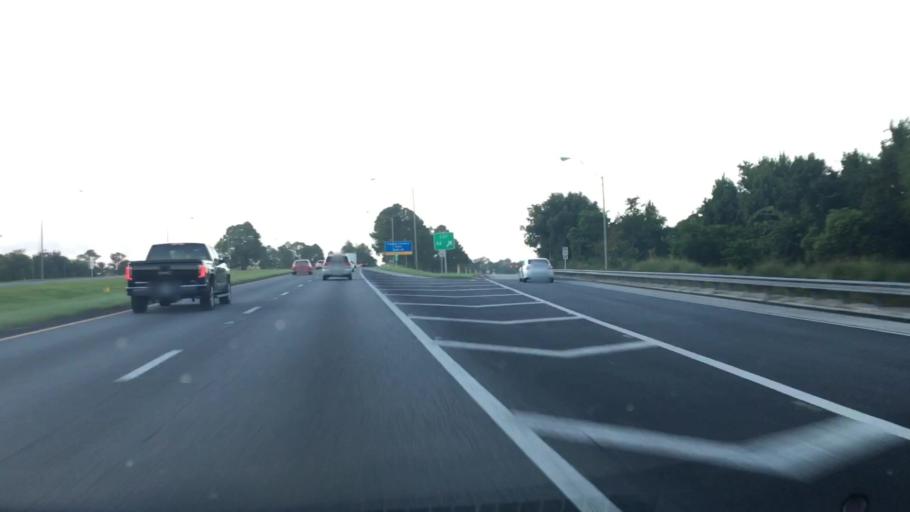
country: US
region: Florida
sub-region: Seminole County
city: Oviedo
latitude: 28.6935
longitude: -81.2308
